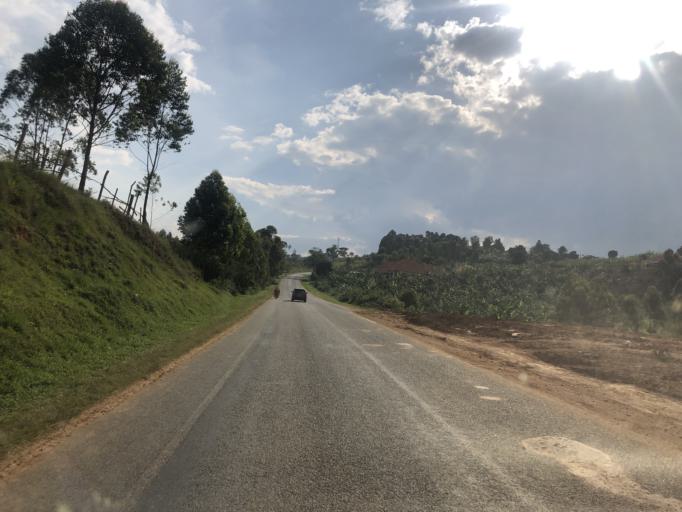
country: UG
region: Western Region
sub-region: Bushenyi District
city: Bushenyi
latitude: -0.5431
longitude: 30.2090
